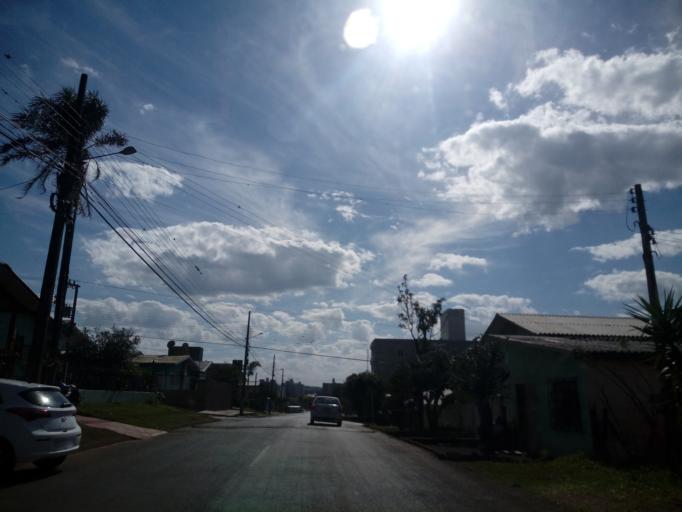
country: BR
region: Santa Catarina
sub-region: Chapeco
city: Chapeco
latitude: -27.1009
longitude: -52.6699
